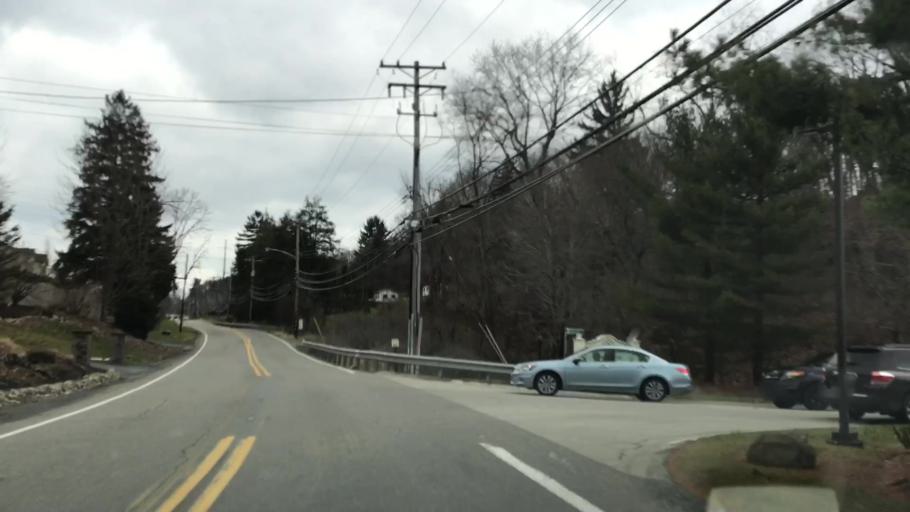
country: US
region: Pennsylvania
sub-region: Allegheny County
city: Rennerdale
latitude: 40.4102
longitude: -80.1145
